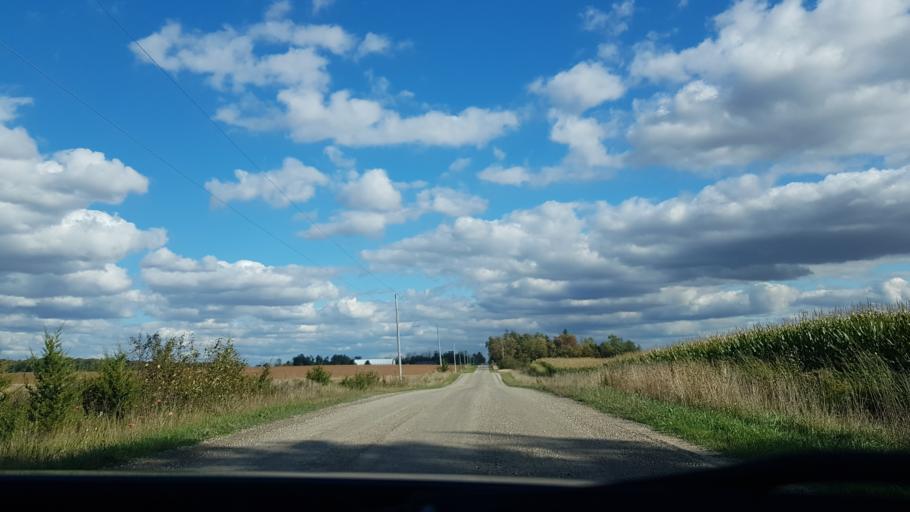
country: CA
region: Ontario
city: South Huron
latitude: 43.1130
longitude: -81.6501
